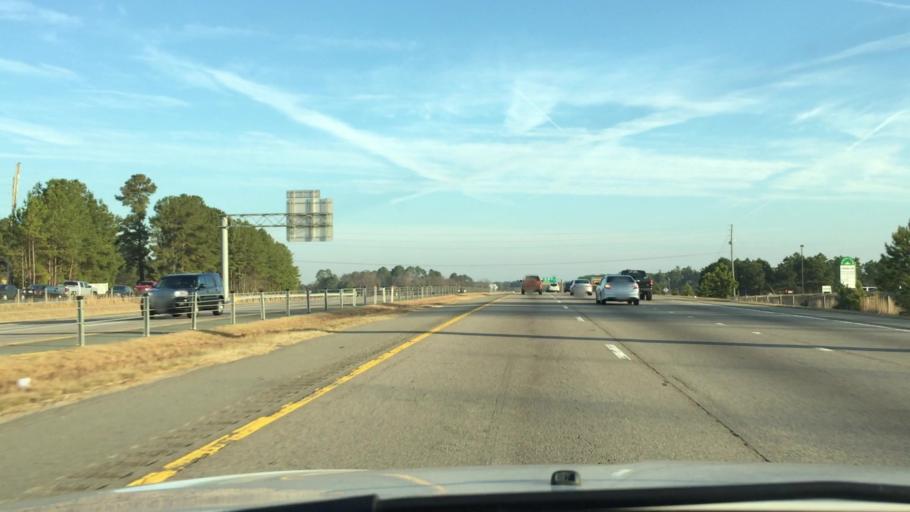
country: US
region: North Carolina
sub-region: Lee County
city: Sanford
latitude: 35.5192
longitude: -79.1852
